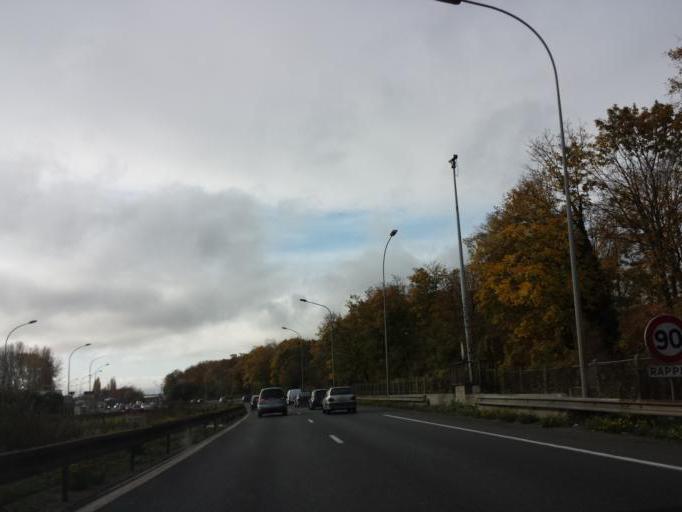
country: FR
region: Ile-de-France
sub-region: Departement du Val-d'Oise
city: Bezons
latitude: 48.9231
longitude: 2.2282
